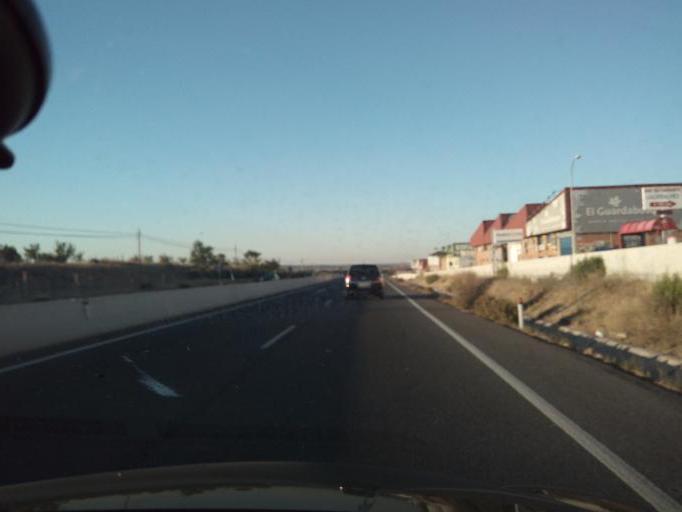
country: ES
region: Madrid
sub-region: Provincia de Madrid
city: Ajalvir
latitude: 40.5020
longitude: -3.4795
